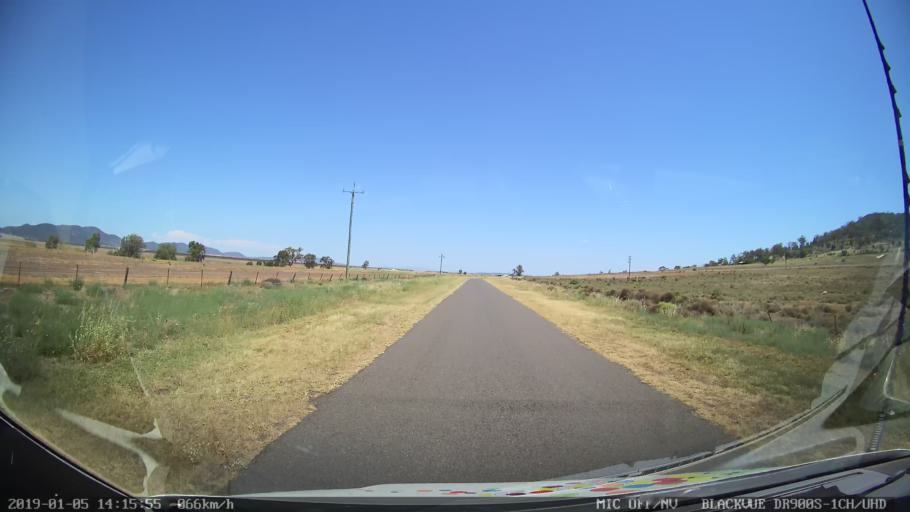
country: AU
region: New South Wales
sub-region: Liverpool Plains
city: Quirindi
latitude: -31.2516
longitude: 150.4719
